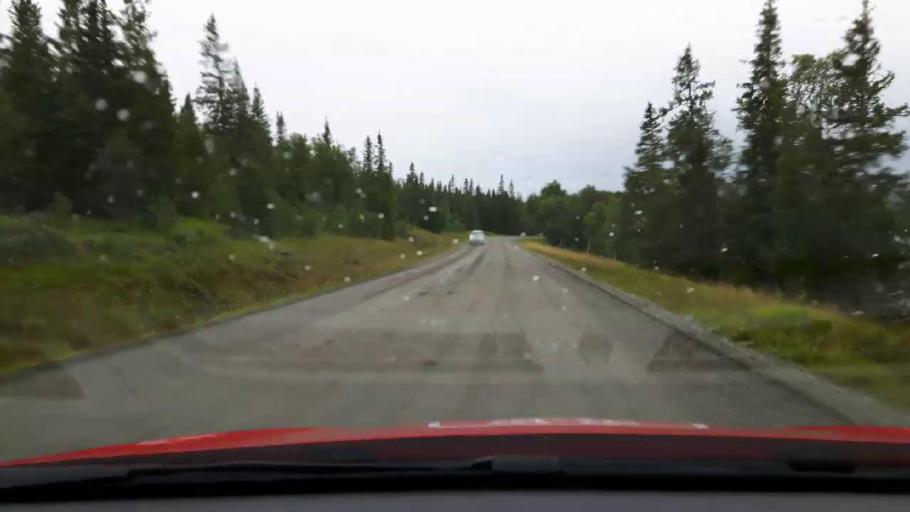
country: NO
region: Nord-Trondelag
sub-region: Meraker
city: Meraker
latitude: 63.5472
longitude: 12.3777
